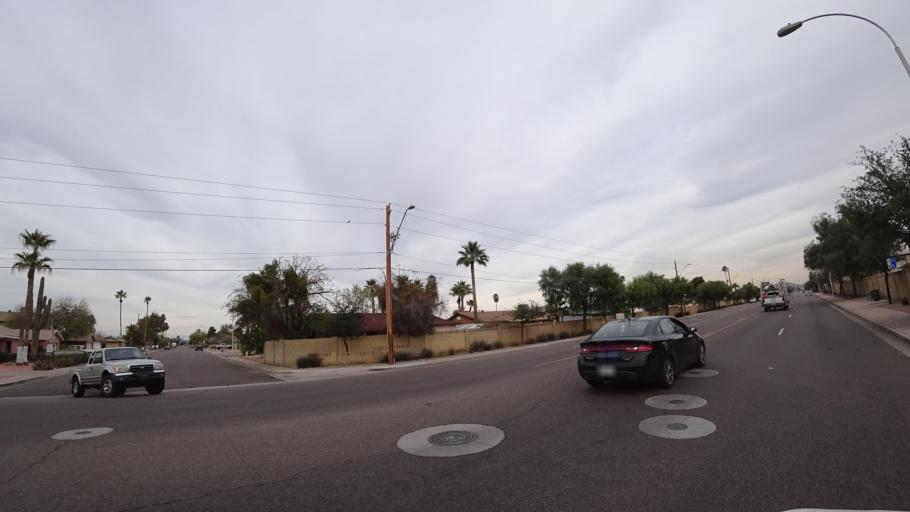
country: US
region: Arizona
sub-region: Maricopa County
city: Glendale
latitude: 33.5818
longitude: -112.1645
